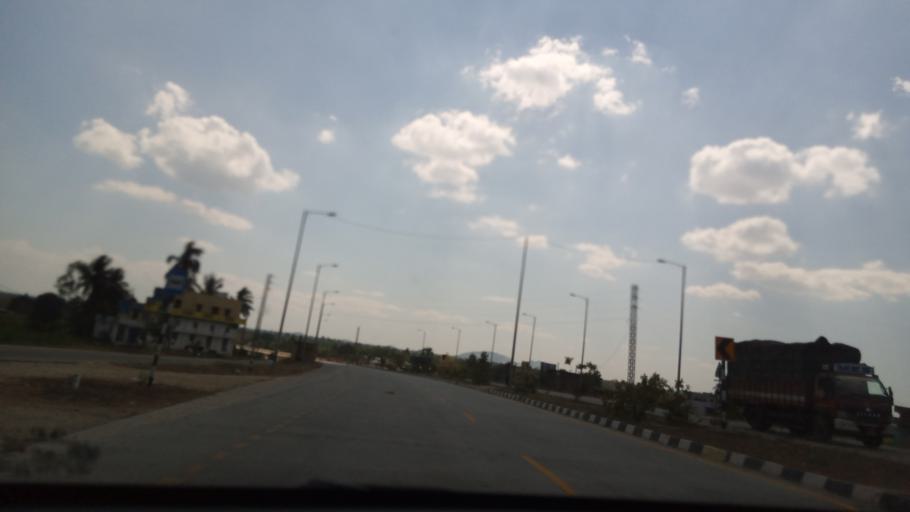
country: IN
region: Andhra Pradesh
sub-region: Chittoor
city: Palmaner
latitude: 13.2196
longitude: 78.7285
